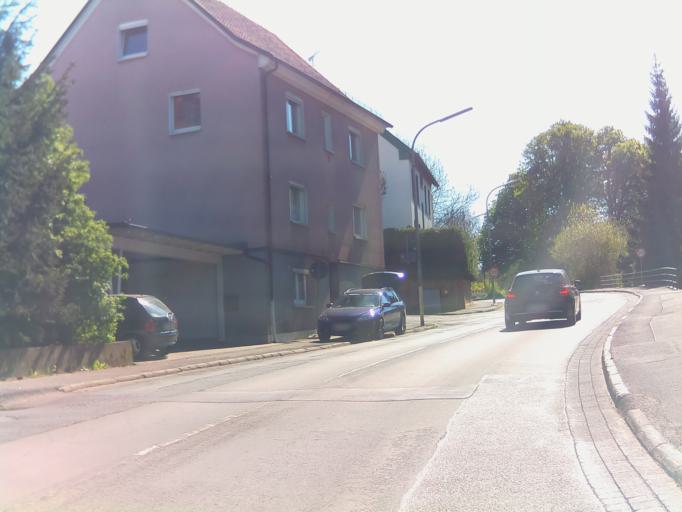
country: DE
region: Hesse
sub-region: Regierungsbezirk Giessen
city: Lauterbach
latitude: 50.6194
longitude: 9.3913
